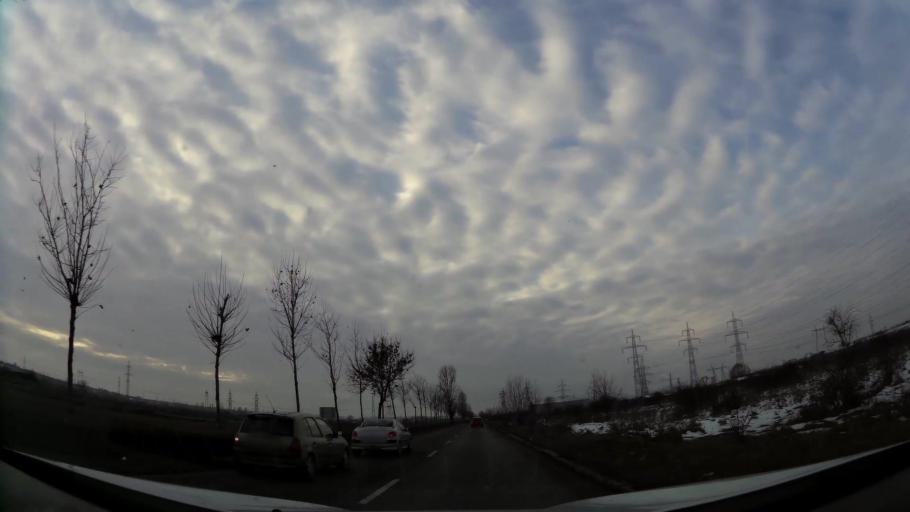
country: RO
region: Ilfov
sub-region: Comuna Popesti-Leordeni
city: Popesti-Leordeni
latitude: 44.3947
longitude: 26.1914
